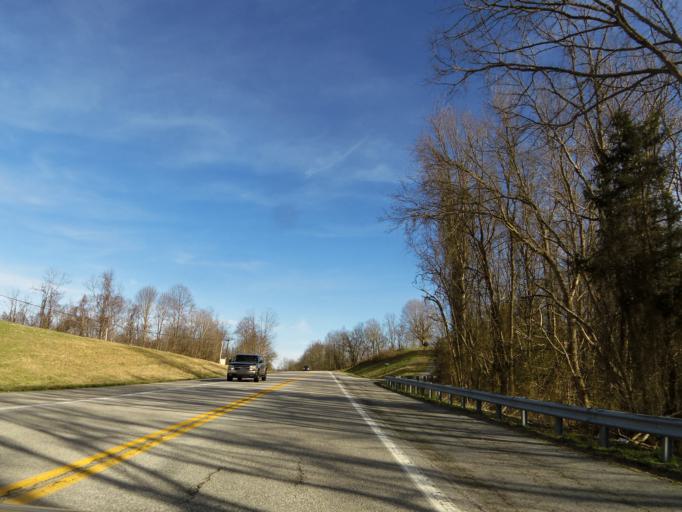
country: US
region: Tennessee
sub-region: Cannon County
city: Woodbury
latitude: 35.8037
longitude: -86.0093
